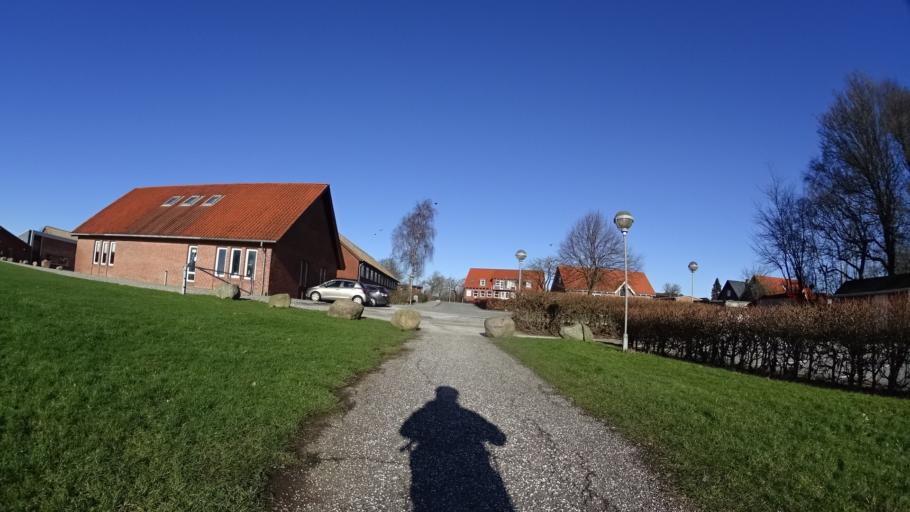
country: DK
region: Central Jutland
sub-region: Arhus Kommune
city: Kolt
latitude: 56.1059
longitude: 10.0967
